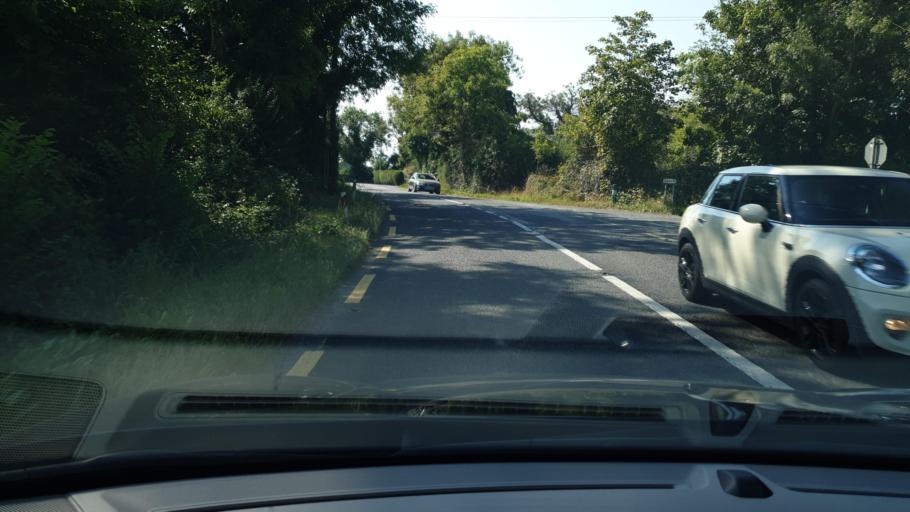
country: IE
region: Leinster
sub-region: An Mhi
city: Dunshaughlin
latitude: 53.5220
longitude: -6.5129
